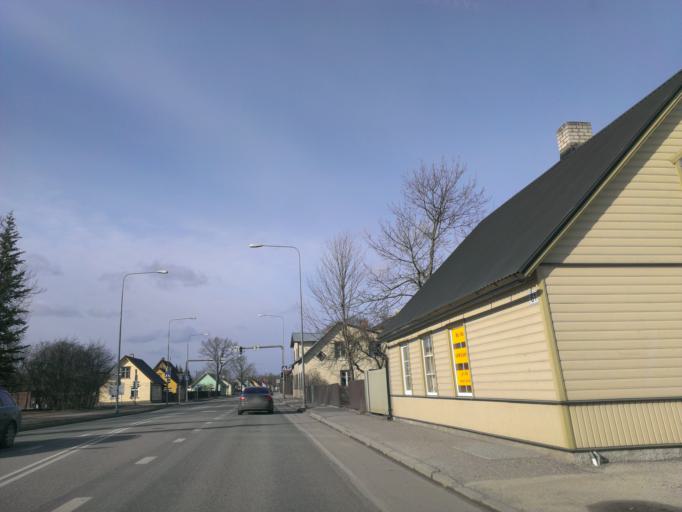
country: EE
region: Paernumaa
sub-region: Paernu linn
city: Parnu
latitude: 58.3984
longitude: 24.4936
